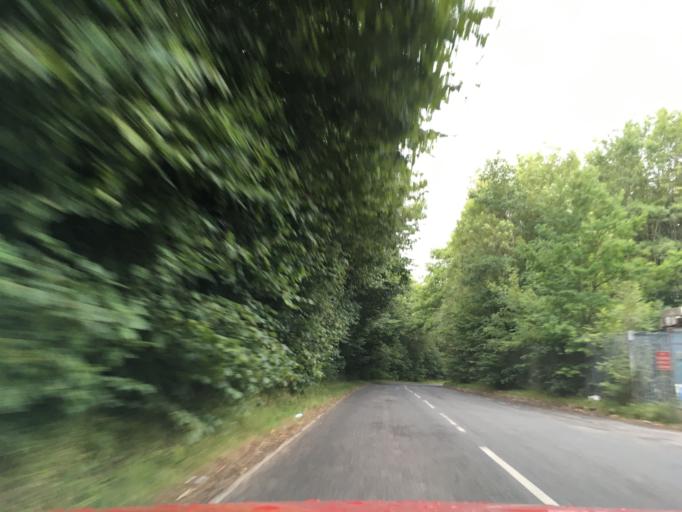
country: GB
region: Wales
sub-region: Newport
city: Langstone
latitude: 51.6241
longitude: -2.9015
